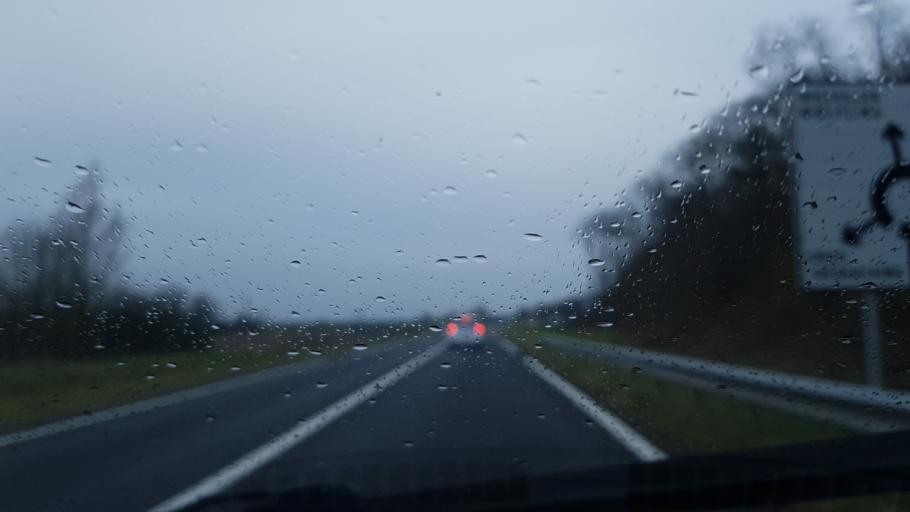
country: FR
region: Lorraine
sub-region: Departement de la Moselle
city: Bliesbruck
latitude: 49.0928
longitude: 7.1976
